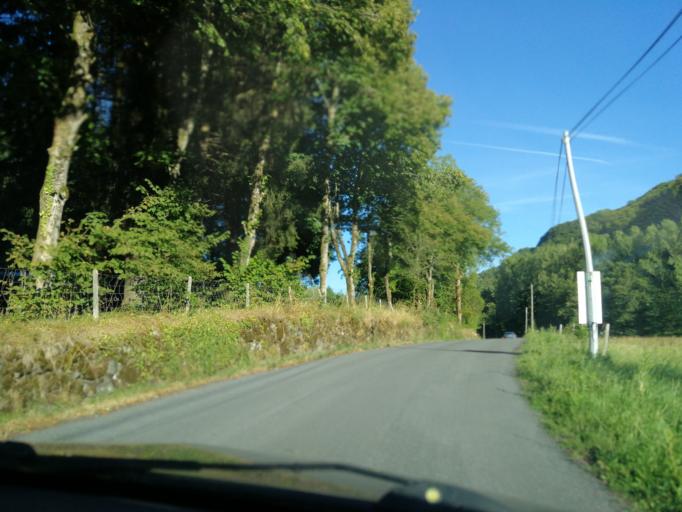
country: FR
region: Auvergne
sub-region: Departement du Cantal
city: Saint-Cernin
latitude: 45.1099
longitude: 2.5085
